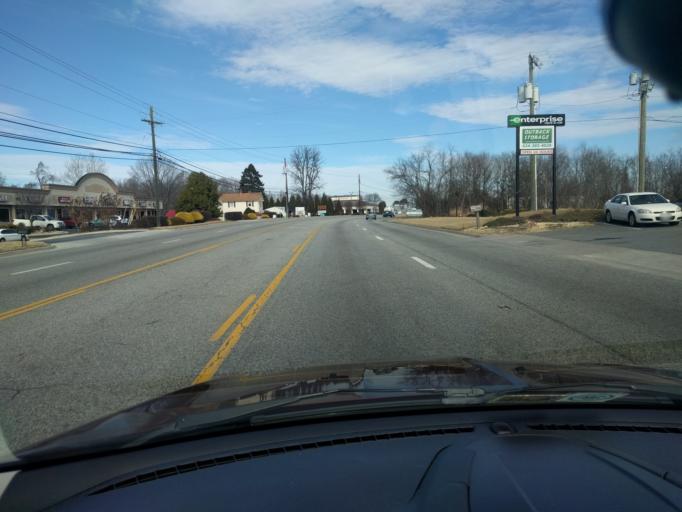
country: US
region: Virginia
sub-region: Bedford County
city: Forest
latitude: 37.3820
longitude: -79.2464
